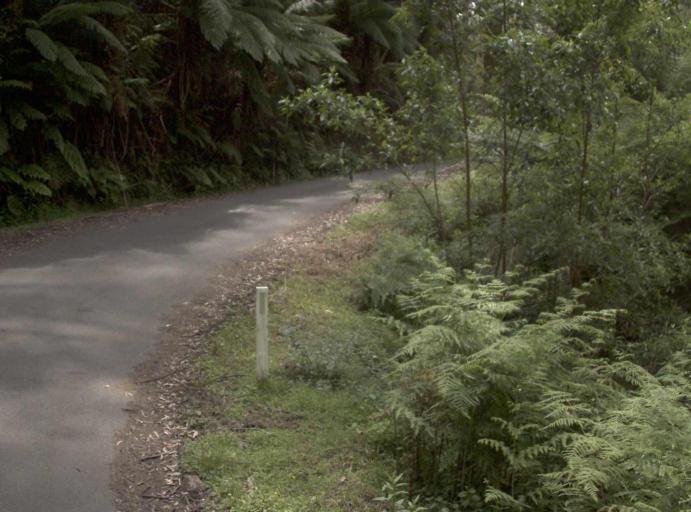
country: AU
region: Victoria
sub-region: Latrobe
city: Traralgon
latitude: -38.4391
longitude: 146.5327
